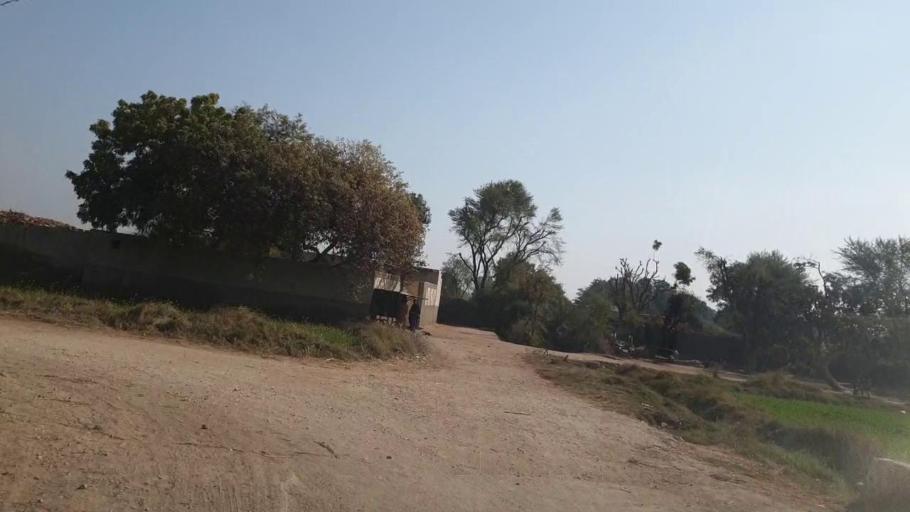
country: PK
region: Sindh
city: Matiari
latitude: 25.5444
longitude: 68.4979
